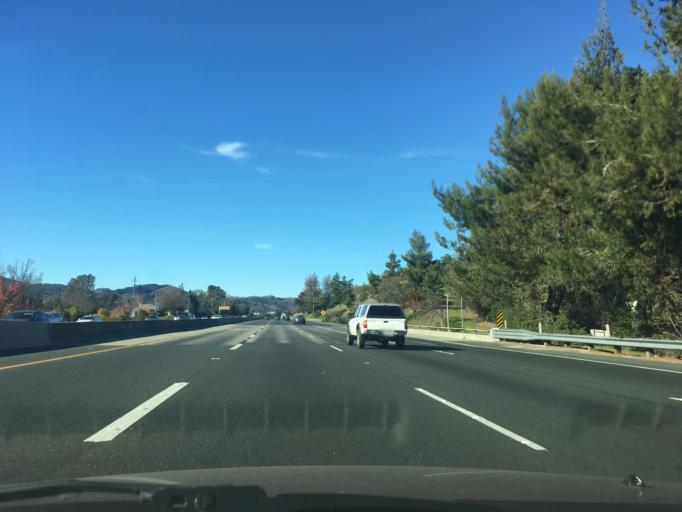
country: US
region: California
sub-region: Contra Costa County
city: Danville
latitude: 37.8345
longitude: -122.0082
